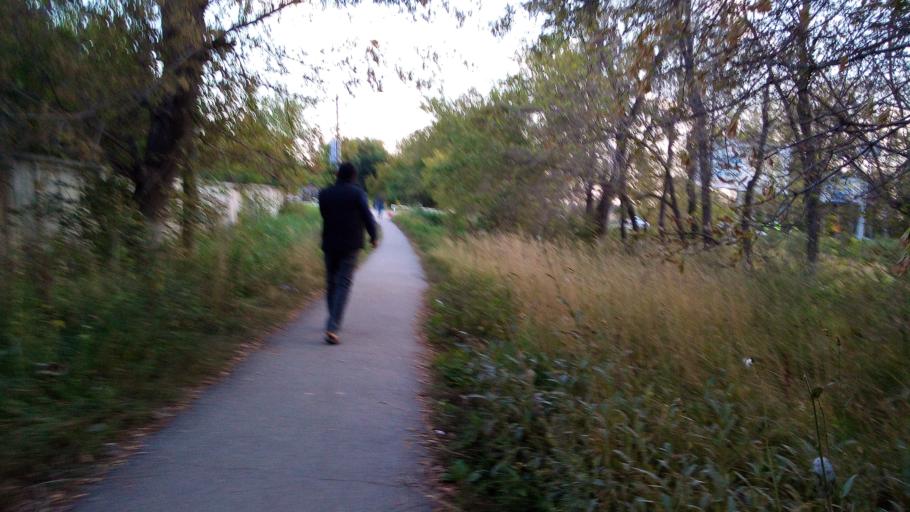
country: RU
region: Chelyabinsk
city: Potanino
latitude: 55.2958
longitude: 61.5124
